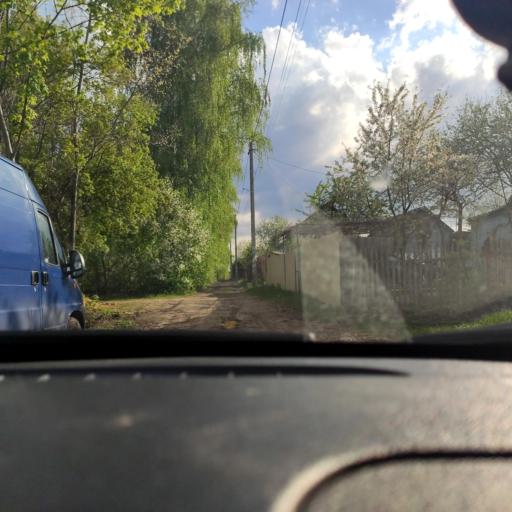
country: RU
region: Voronezj
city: Voronezh
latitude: 51.5992
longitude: 39.1548
